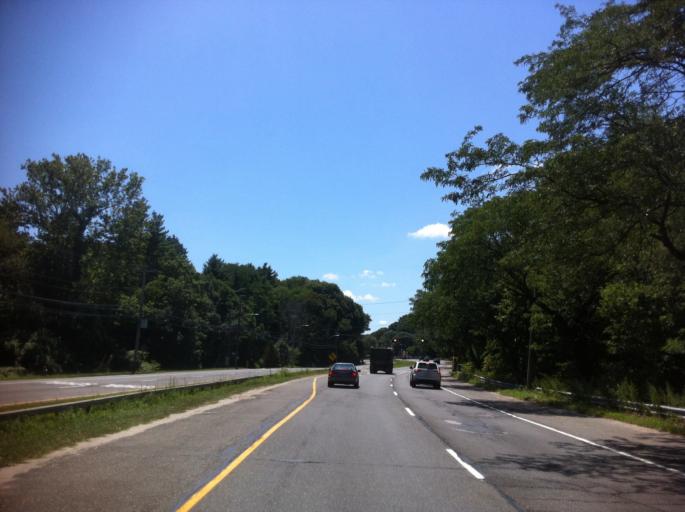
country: US
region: New York
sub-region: Nassau County
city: Glen Head
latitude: 40.8501
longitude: -73.6180
